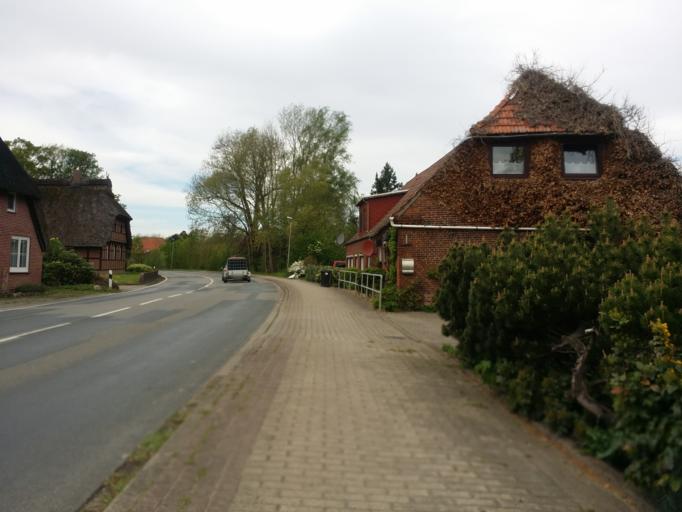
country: DE
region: Lower Saxony
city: Lemwerder
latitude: 53.1415
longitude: 8.5727
